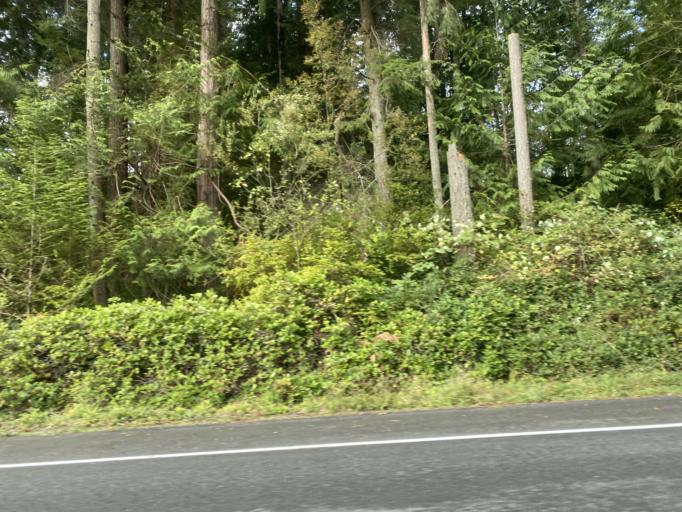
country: US
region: Washington
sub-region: Island County
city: Langley
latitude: 48.0171
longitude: -122.4095
